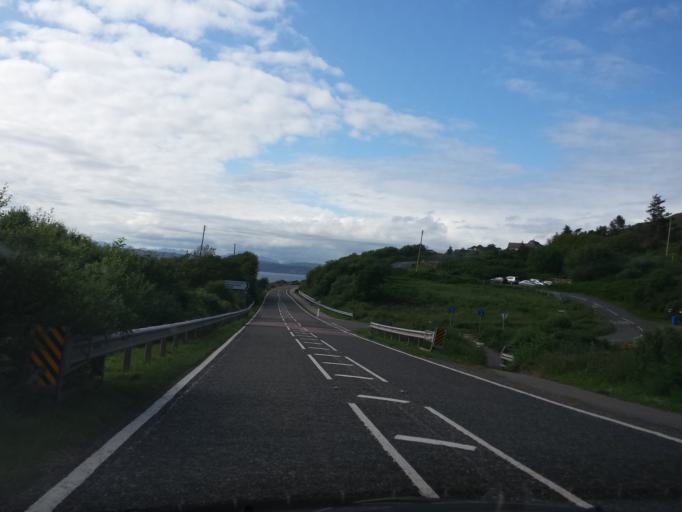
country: GB
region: Scotland
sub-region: Argyll and Bute
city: Isle Of Mull
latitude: 56.9922
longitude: -5.8285
